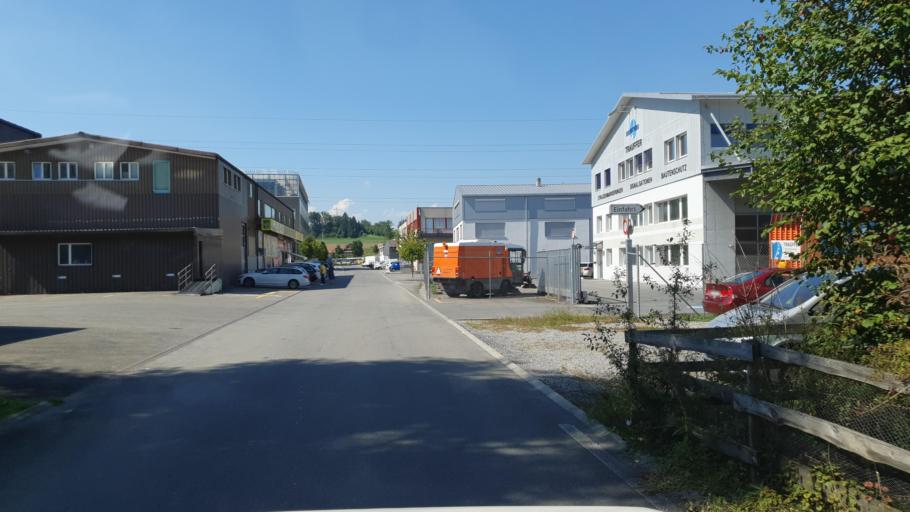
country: CH
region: Lucerne
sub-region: Lucerne-Land District
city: Buchrain
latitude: 47.1091
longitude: 8.3273
